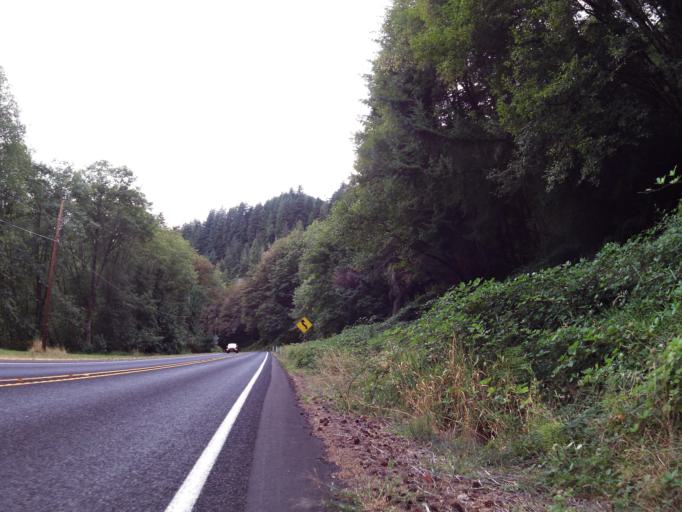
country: US
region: Oregon
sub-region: Columbia County
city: Clatskanie
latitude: 46.1731
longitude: -123.2297
